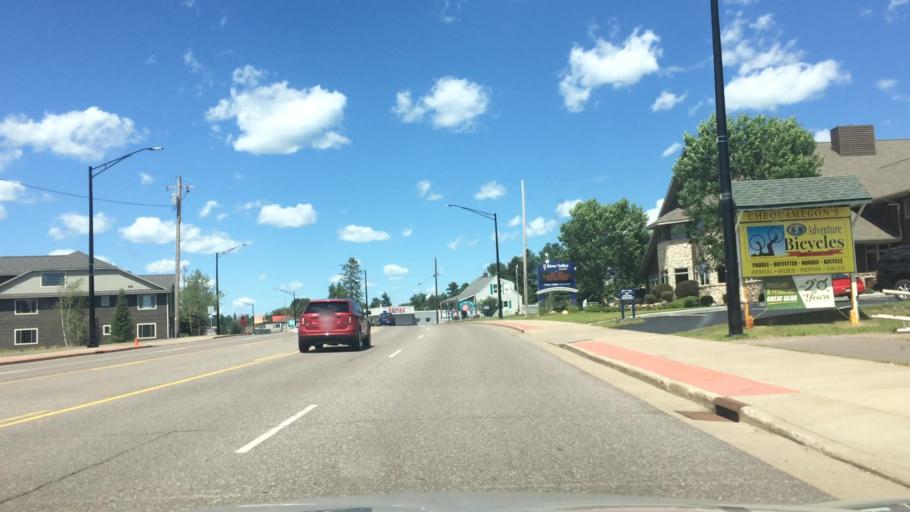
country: US
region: Wisconsin
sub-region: Vilas County
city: Lac du Flambeau
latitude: 45.8798
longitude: -89.7030
